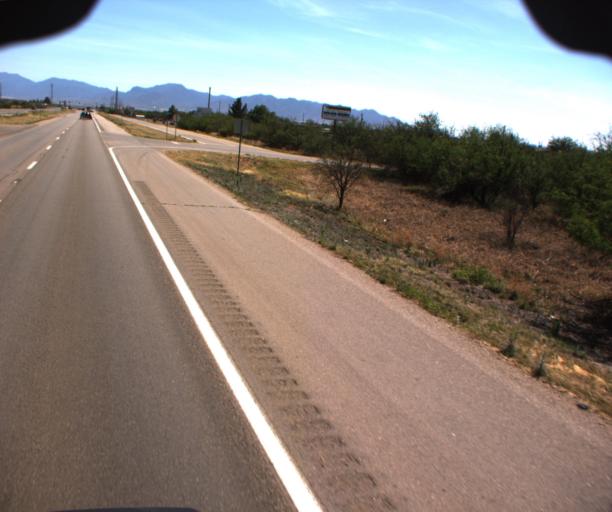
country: US
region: Arizona
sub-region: Cochise County
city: Huachuca City
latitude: 31.6983
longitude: -110.3504
